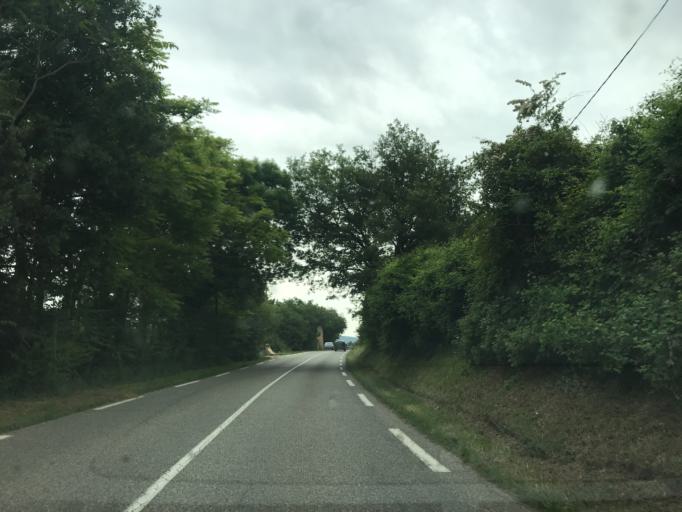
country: FR
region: Provence-Alpes-Cote d'Azur
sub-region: Departement du Var
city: Rians
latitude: 43.6273
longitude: 5.7686
